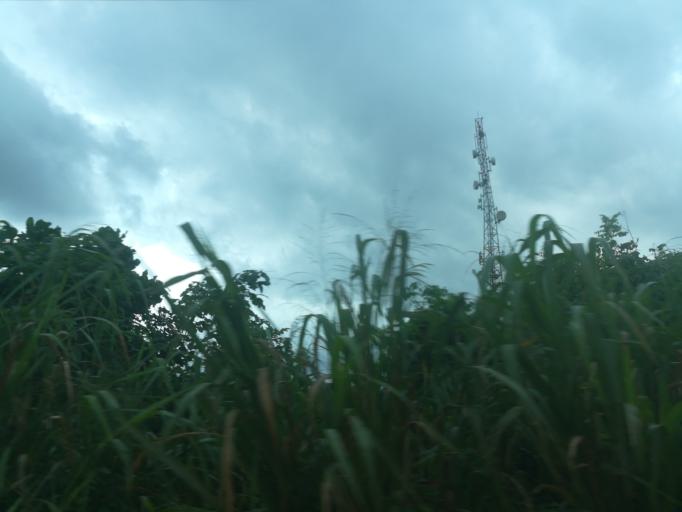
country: NG
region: Lagos
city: Ikorodu
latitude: 6.6637
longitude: 3.5992
